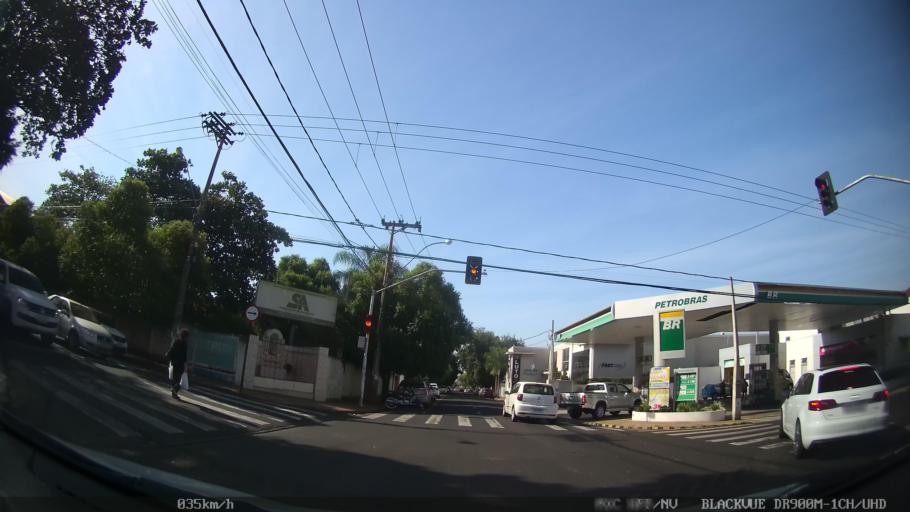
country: BR
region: Sao Paulo
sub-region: Sao Jose Do Rio Preto
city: Sao Jose do Rio Preto
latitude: -20.8035
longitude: -49.3859
